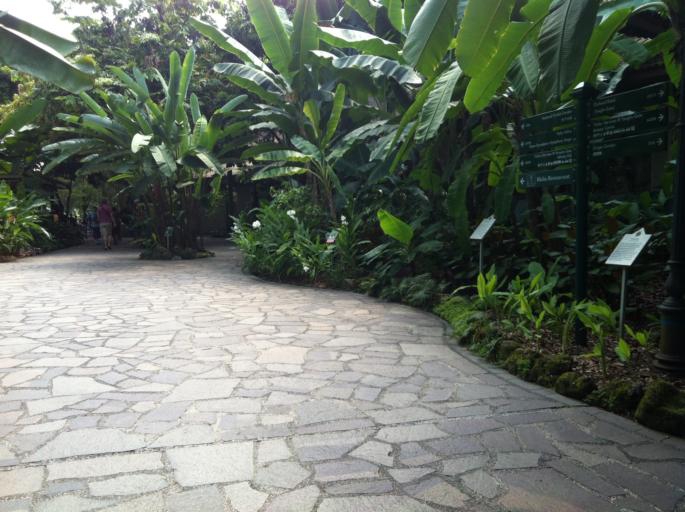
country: SG
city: Singapore
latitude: 1.3111
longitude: 103.8152
